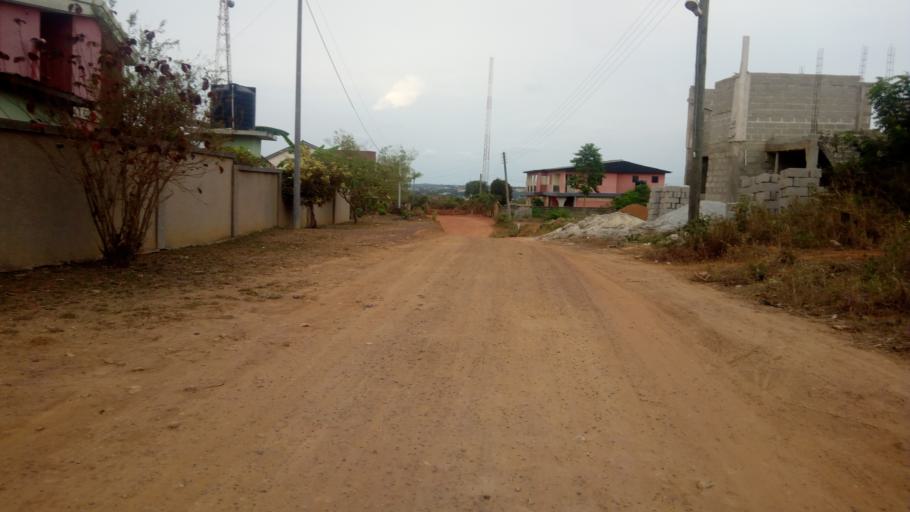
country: GH
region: Central
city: Cape Coast
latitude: 5.1106
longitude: -1.2768
